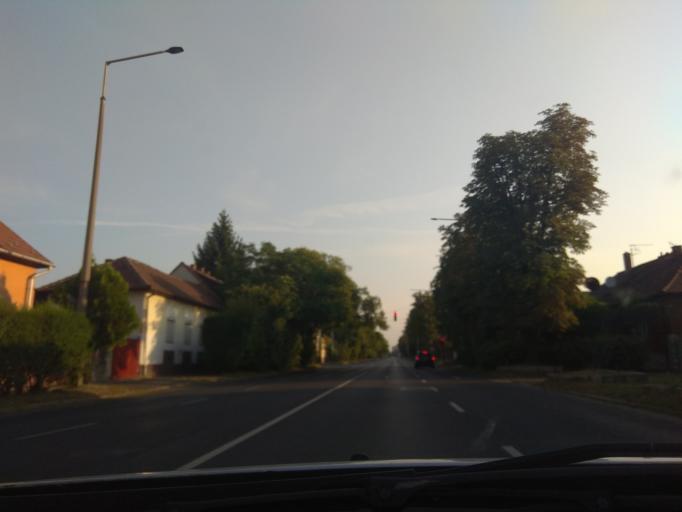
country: HU
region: Borsod-Abauj-Zemplen
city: Miskolc
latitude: 48.0889
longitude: 20.7919
